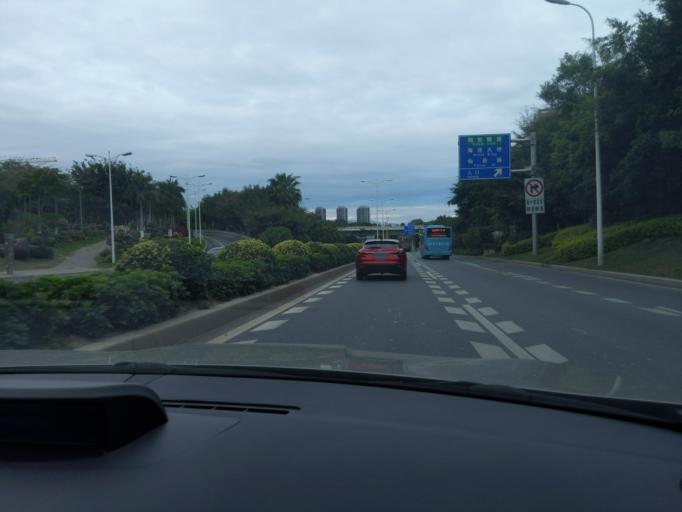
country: CN
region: Fujian
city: Liuwudian
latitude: 24.5128
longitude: 118.1814
